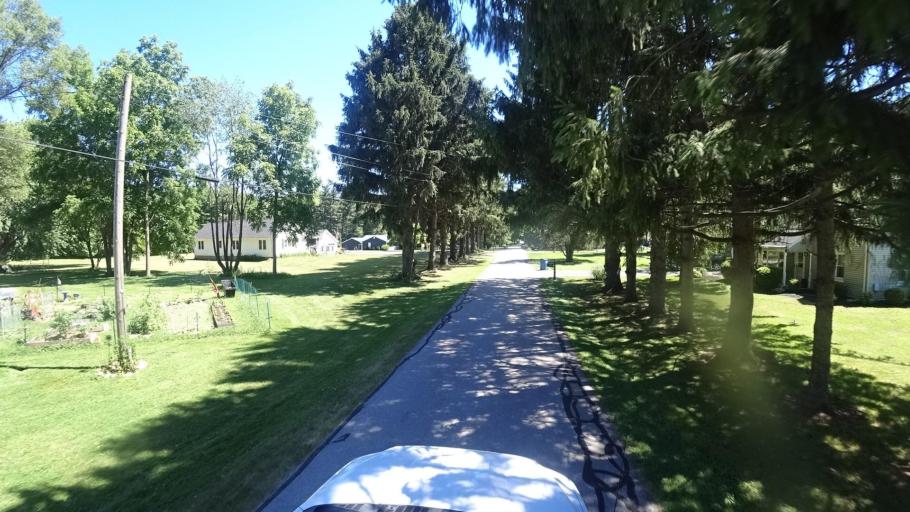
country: US
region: Indiana
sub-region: Porter County
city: Porter
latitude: 41.6256
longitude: -87.0807
